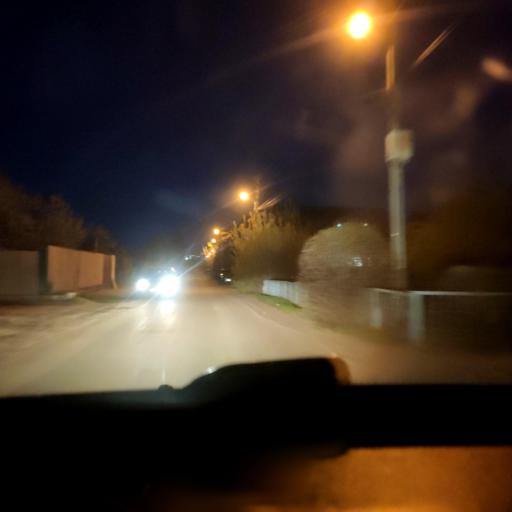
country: RU
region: Voronezj
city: Voronezh
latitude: 51.7439
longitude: 39.2610
